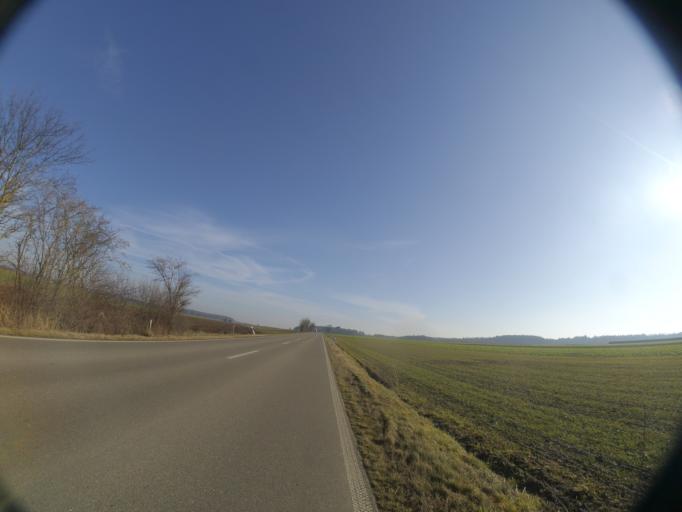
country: DE
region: Baden-Wuerttemberg
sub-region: Tuebingen Region
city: Dornstadt
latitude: 48.4866
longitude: 9.9405
